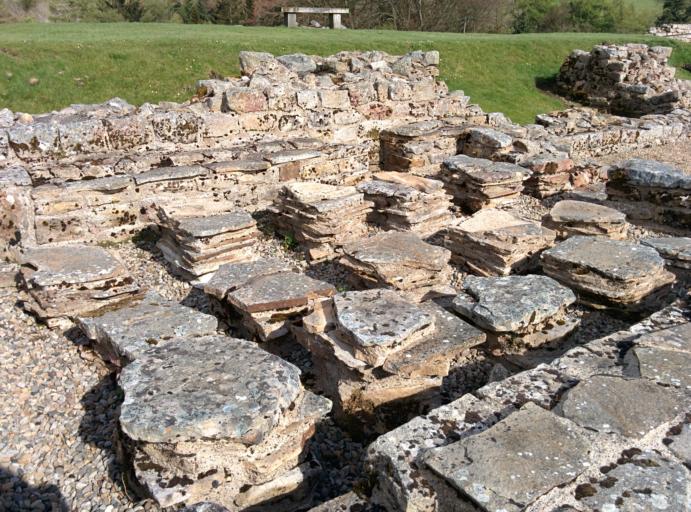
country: GB
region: England
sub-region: Northumberland
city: Bardon Mill
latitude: 54.9913
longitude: -2.3597
